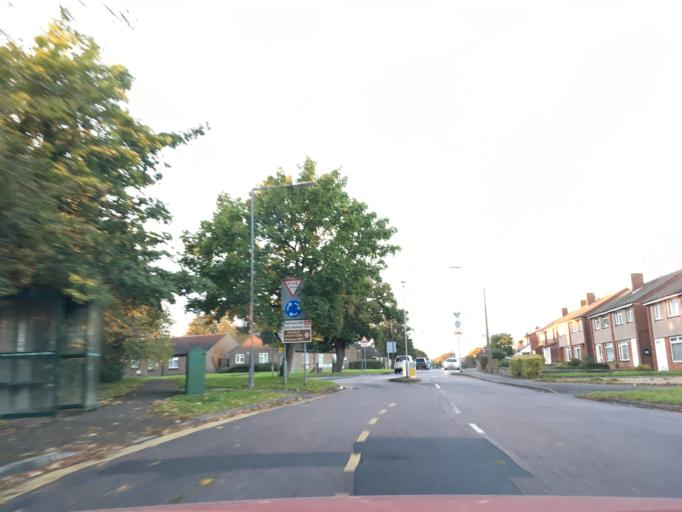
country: GB
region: England
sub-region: South Gloucestershire
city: Stoke Gifford
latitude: 51.5298
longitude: -2.5599
